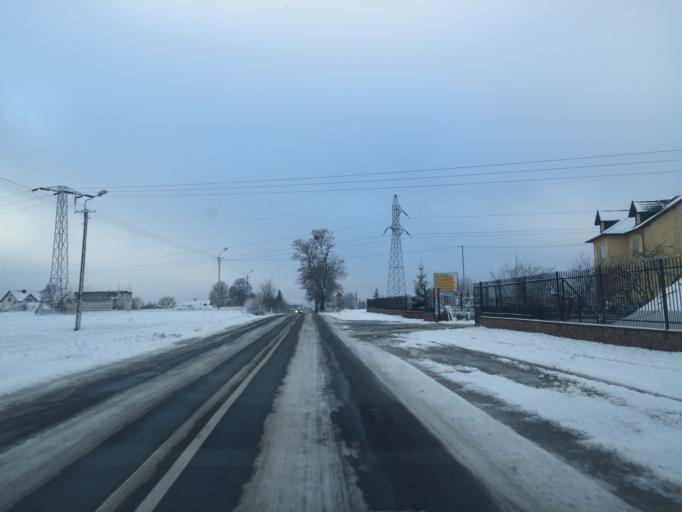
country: PL
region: Kujawsko-Pomorskie
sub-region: Powiat brodnicki
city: Brodnica
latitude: 53.2429
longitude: 19.4744
